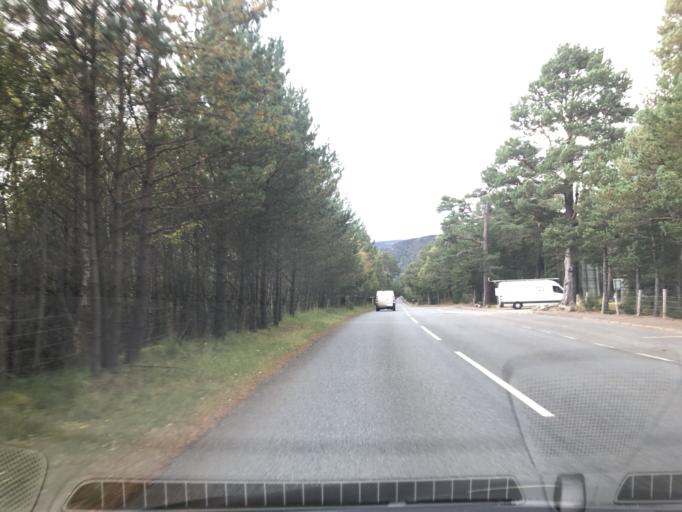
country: GB
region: Scotland
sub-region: Highland
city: Aviemore
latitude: 57.1734
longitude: -3.8032
